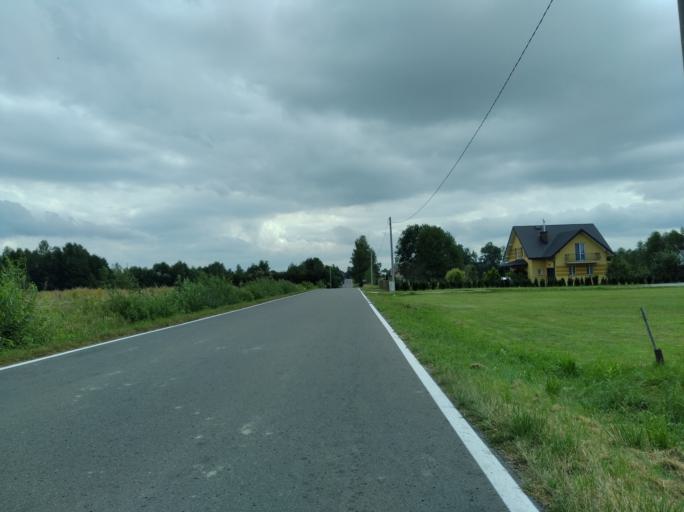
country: PL
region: Subcarpathian Voivodeship
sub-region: Powiat krosnienski
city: Odrzykon
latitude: 49.7452
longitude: 21.7280
